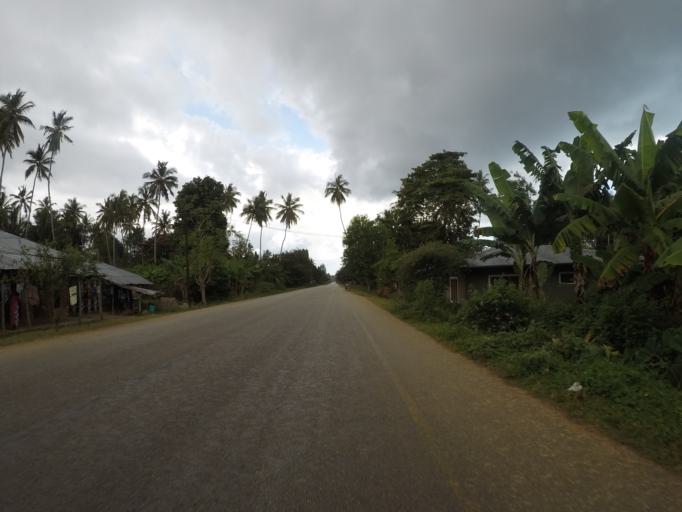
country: TZ
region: Zanzibar North
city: Mkokotoni
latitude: -5.9743
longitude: 39.1963
